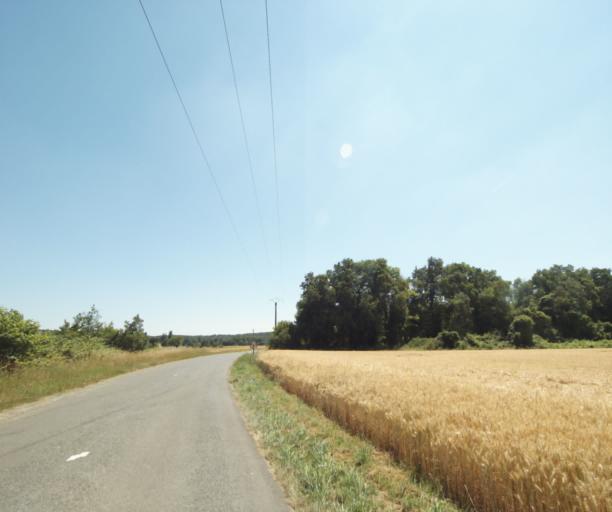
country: FR
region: Ile-de-France
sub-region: Departement de Seine-et-Marne
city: Noisy-sur-Ecole
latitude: 48.3606
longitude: 2.5128
